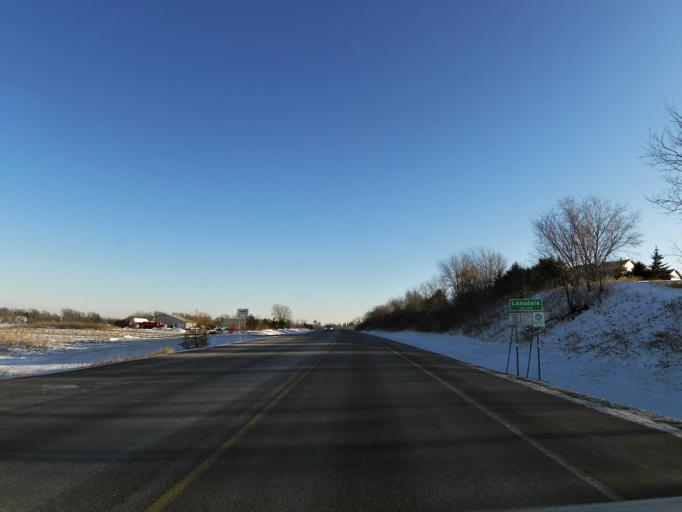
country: US
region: Minnesota
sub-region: Rice County
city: Lonsdale
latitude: 44.4857
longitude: -93.4413
